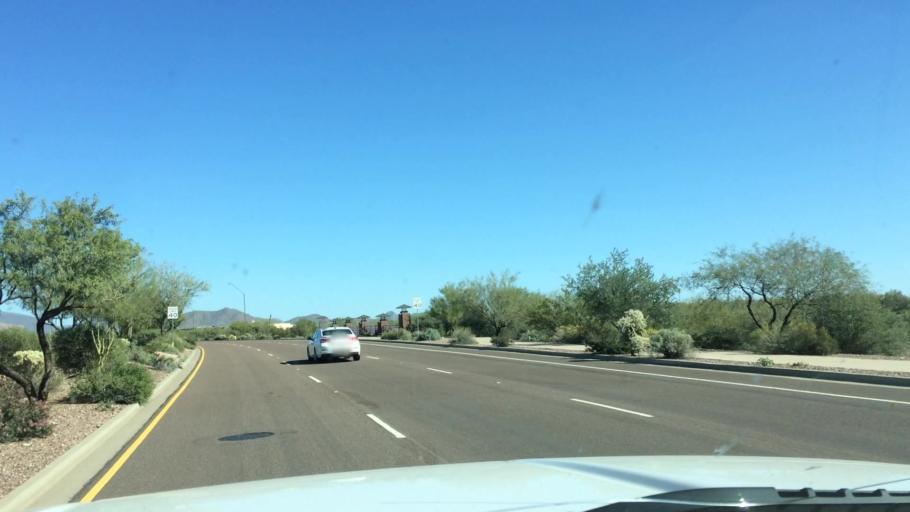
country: US
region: Arizona
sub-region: Maricopa County
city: Anthem
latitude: 33.8433
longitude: -112.1304
